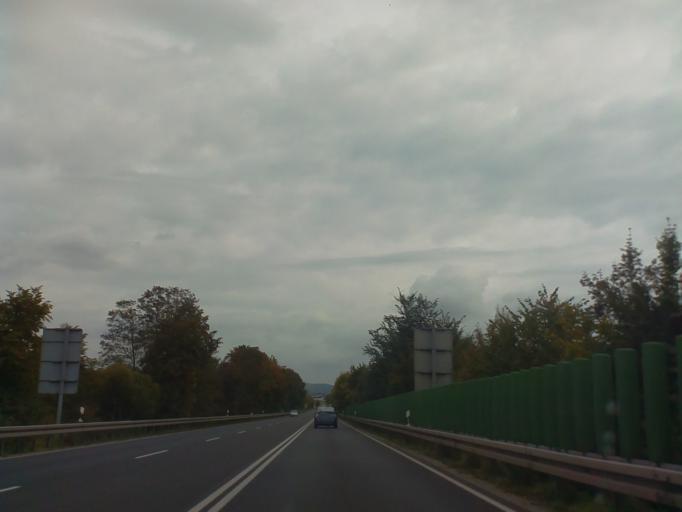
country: DE
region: Hesse
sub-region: Regierungsbezirk Kassel
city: Burghaun
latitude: 50.6981
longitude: 9.7355
